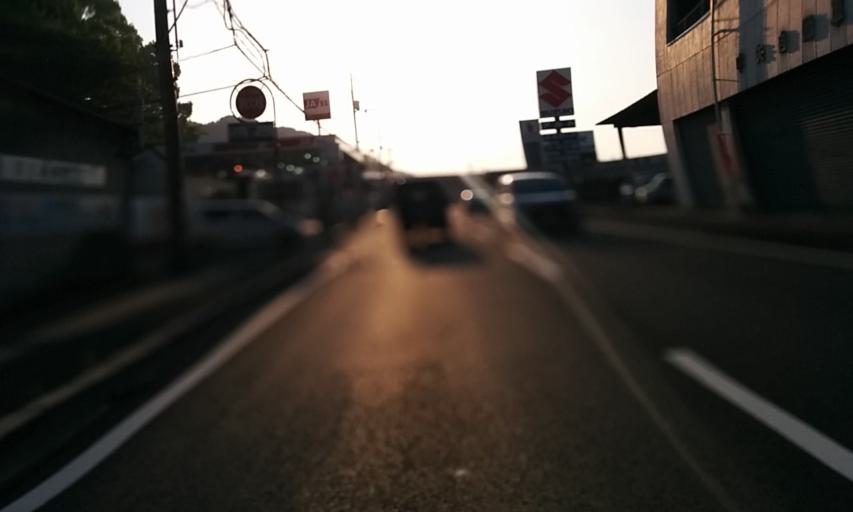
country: JP
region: Ehime
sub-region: Shikoku-chuo Shi
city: Matsuyama
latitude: 33.7815
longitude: 132.7896
